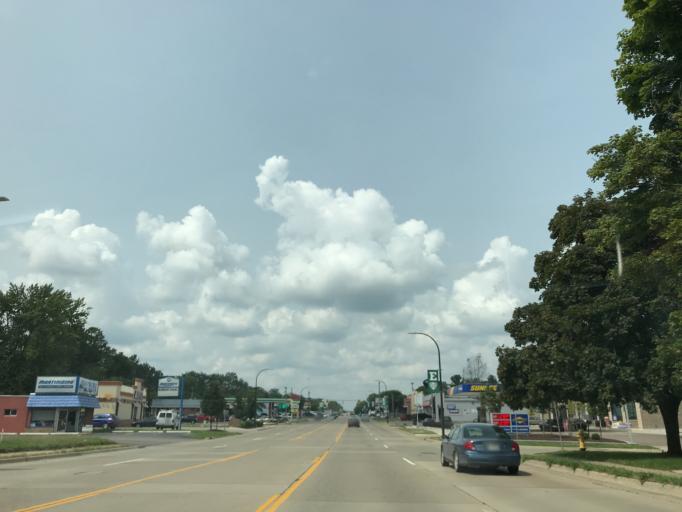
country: US
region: Michigan
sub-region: Washtenaw County
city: Ypsilanti
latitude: 42.2470
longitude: -83.6343
